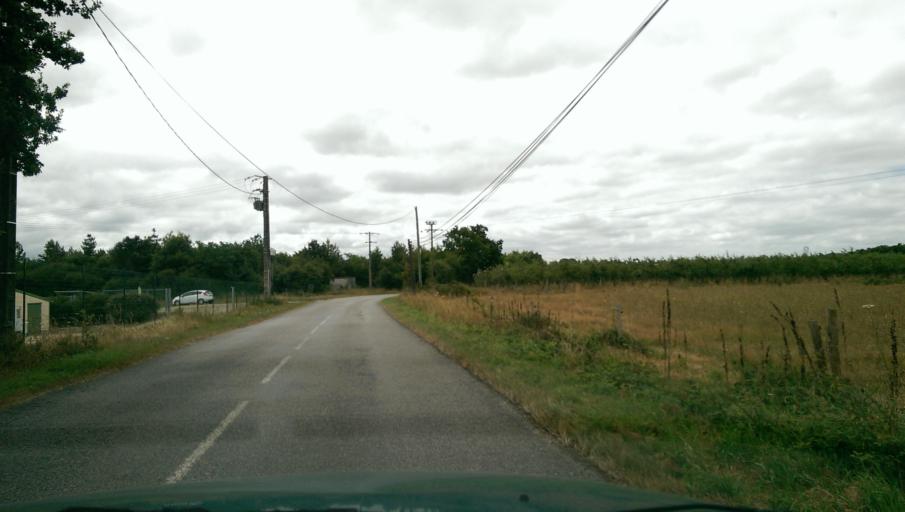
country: FR
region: Pays de la Loire
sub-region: Departement de la Loire-Atlantique
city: La Planche
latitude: 47.0207
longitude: -1.4114
